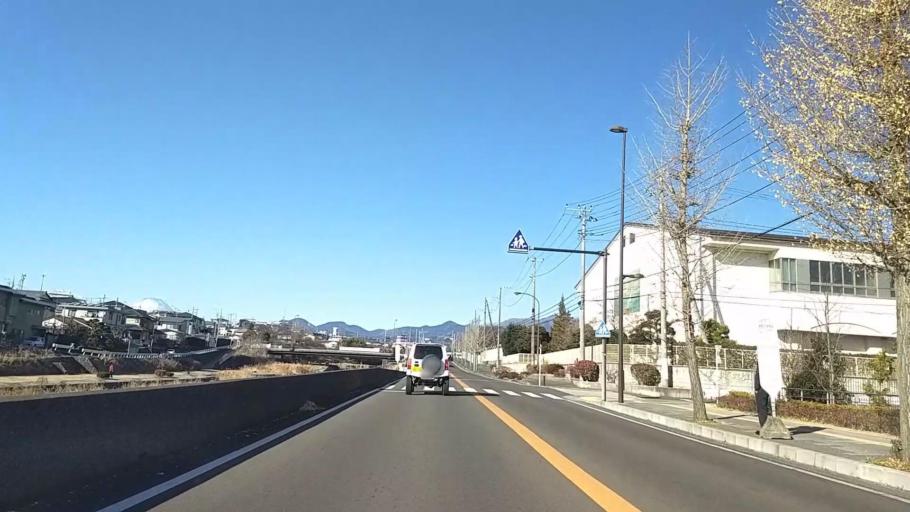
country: JP
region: Kanagawa
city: Hadano
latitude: 35.3753
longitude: 139.2153
